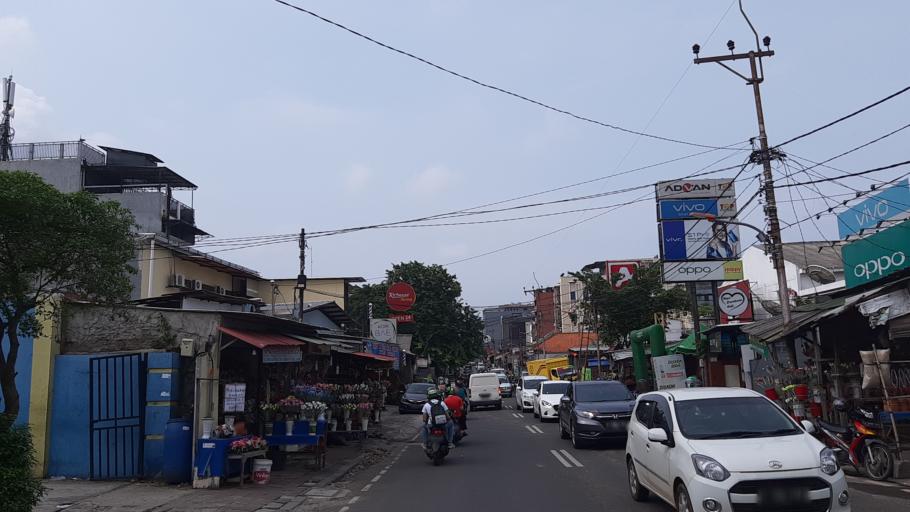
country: ID
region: Jakarta Raya
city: Jakarta
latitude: -6.2056
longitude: 106.7831
